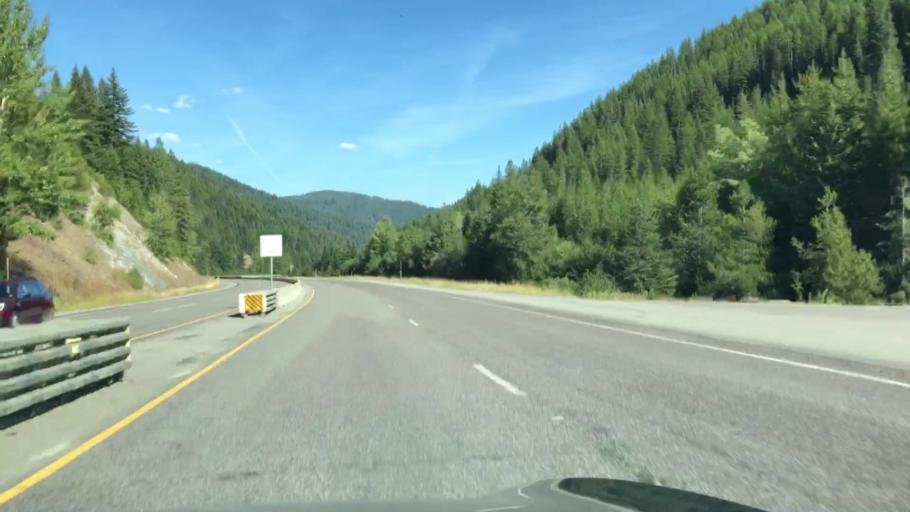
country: US
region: Montana
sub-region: Sanders County
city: Thompson Falls
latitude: 47.4170
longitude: -115.5638
